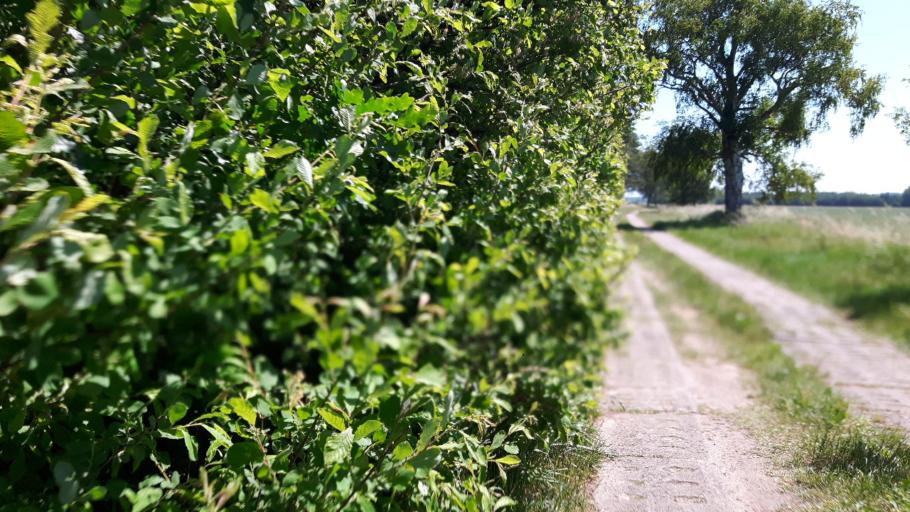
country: PL
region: Pomeranian Voivodeship
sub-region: Powiat slupski
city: Smoldzino
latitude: 54.6710
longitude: 17.1939
